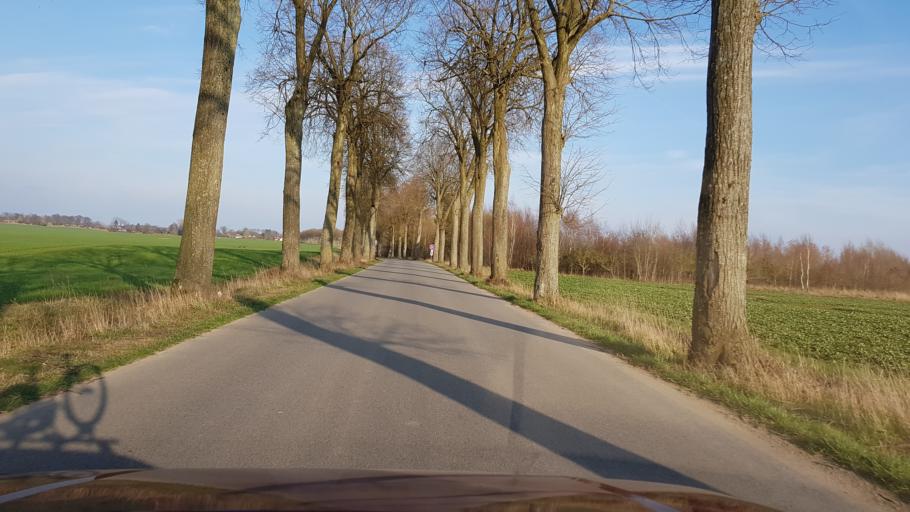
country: PL
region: West Pomeranian Voivodeship
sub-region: Powiat bialogardzki
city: Bialogard
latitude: 54.1225
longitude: 15.9701
